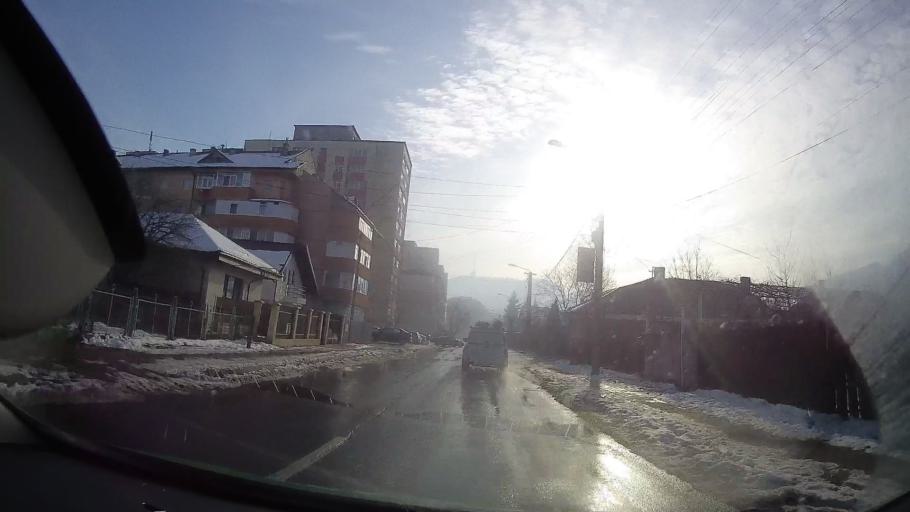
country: RO
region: Neamt
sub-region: Municipiul Piatra-Neamt
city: Valeni
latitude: 46.9436
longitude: 26.3824
